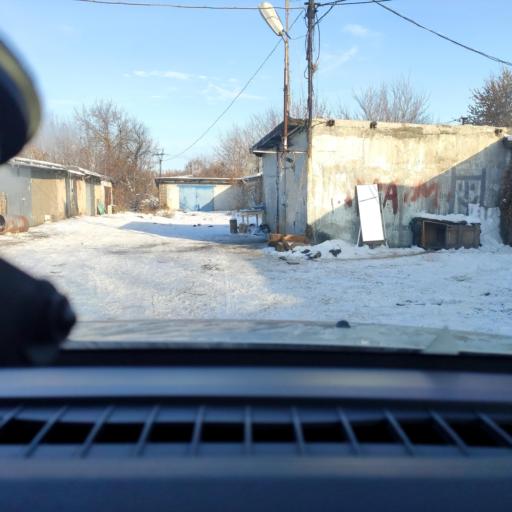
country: RU
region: Samara
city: Chapayevsk
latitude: 52.9901
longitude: 49.7170
